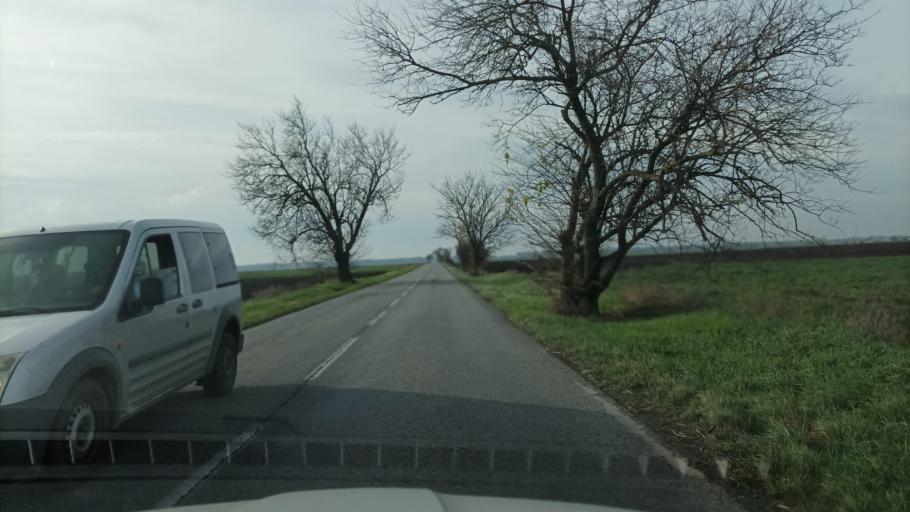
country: HU
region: Pest
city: Rackeve
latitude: 47.1090
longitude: 18.9389
